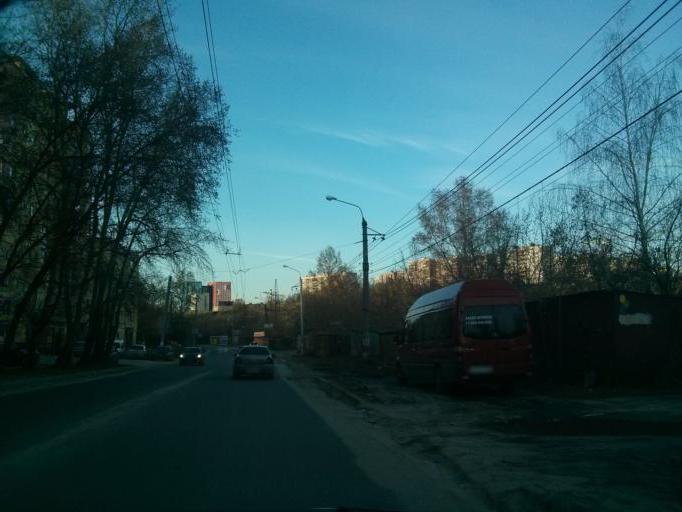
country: RU
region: Nizjnij Novgorod
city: Afonino
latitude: 56.2909
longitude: 44.0530
